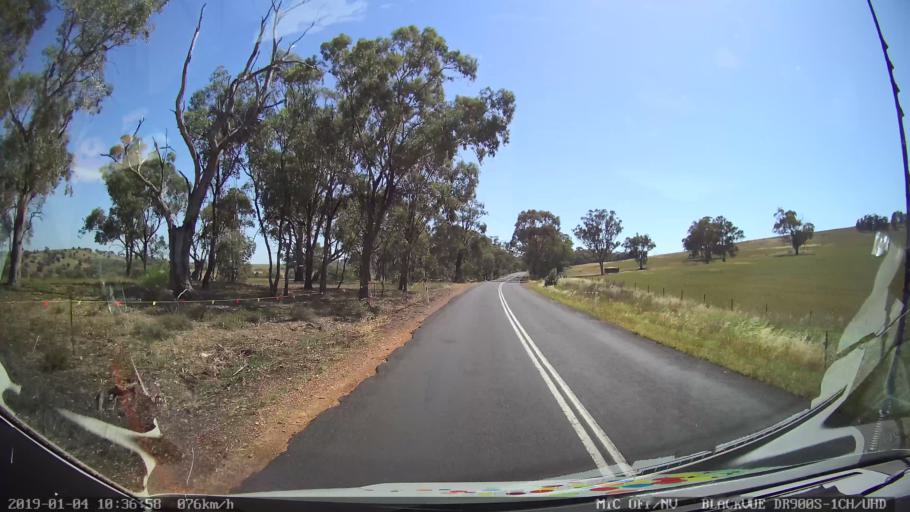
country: AU
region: New South Wales
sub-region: Cabonne
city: Canowindra
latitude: -33.2994
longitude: 148.6897
